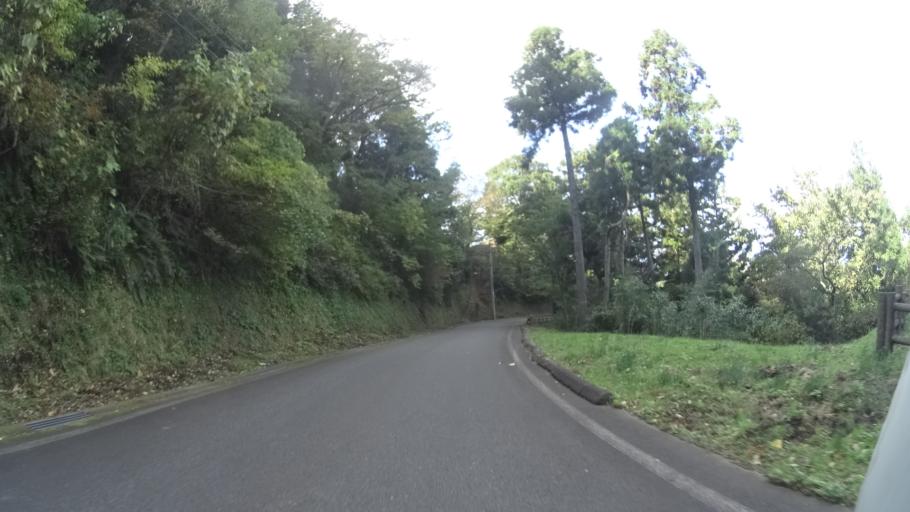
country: JP
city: Asahi
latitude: 35.9805
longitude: 135.9648
